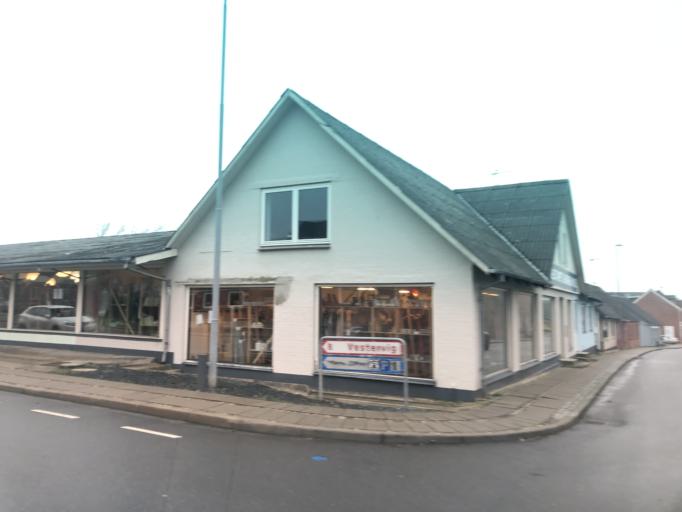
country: DK
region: North Denmark
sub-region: Thisted Kommune
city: Hurup
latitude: 56.7477
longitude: 8.4204
